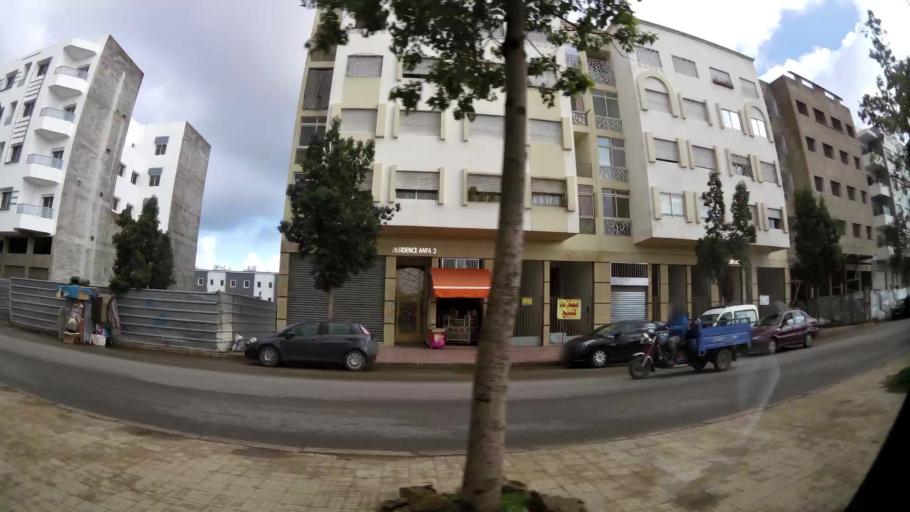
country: MA
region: Grand Casablanca
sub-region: Mediouna
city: Tit Mellil
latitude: 33.5898
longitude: -7.5197
